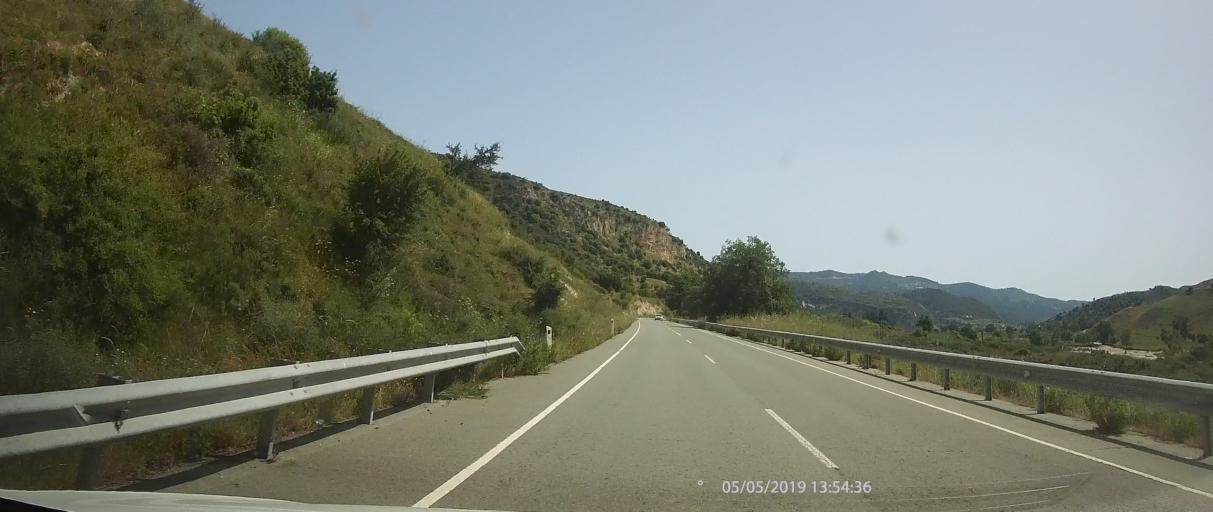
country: CY
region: Limassol
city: Pachna
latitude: 34.8189
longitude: 32.7199
